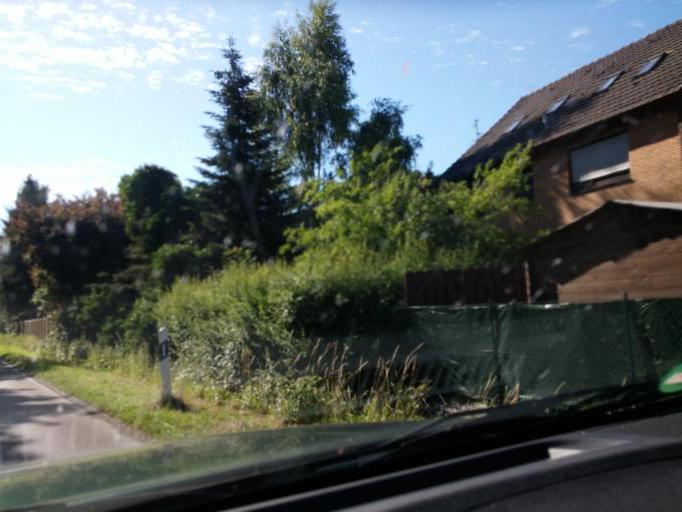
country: DE
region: North Rhine-Westphalia
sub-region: Regierungsbezirk Dusseldorf
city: Monchengladbach
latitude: 51.1370
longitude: 6.3854
